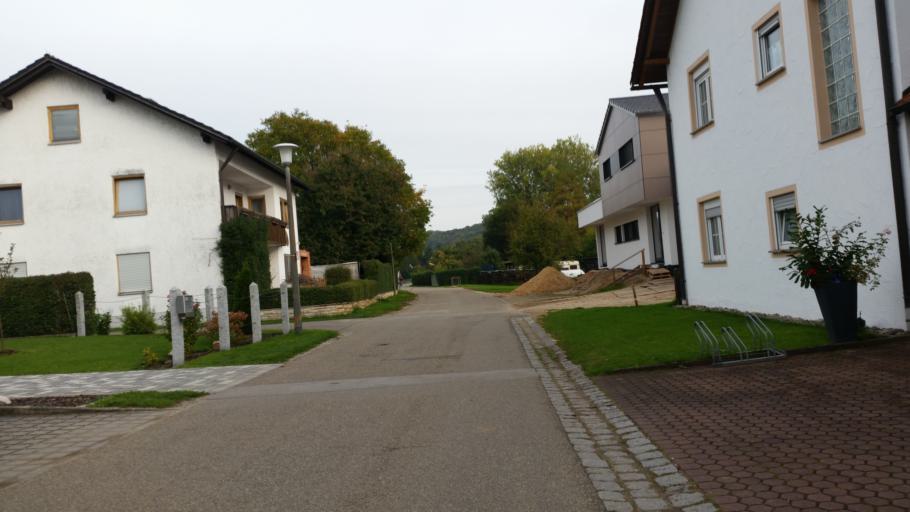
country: DE
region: Bavaria
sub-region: Upper Bavaria
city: Walting
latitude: 48.9226
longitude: 11.3542
